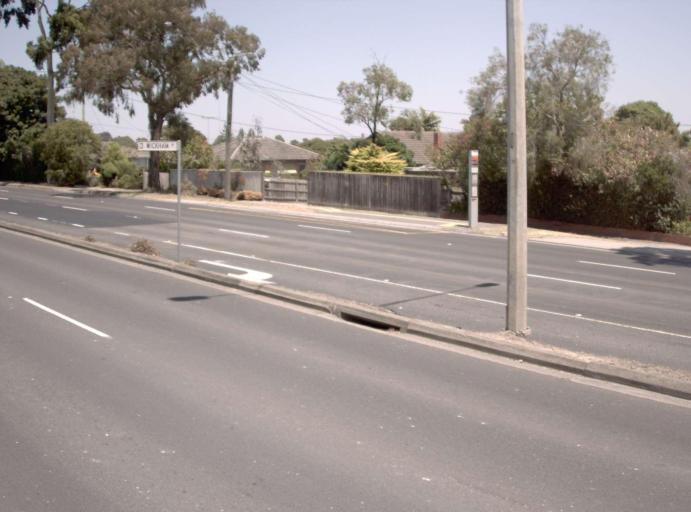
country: AU
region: Victoria
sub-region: Whitehorse
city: Forest Hill
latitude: -37.8313
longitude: 145.1736
